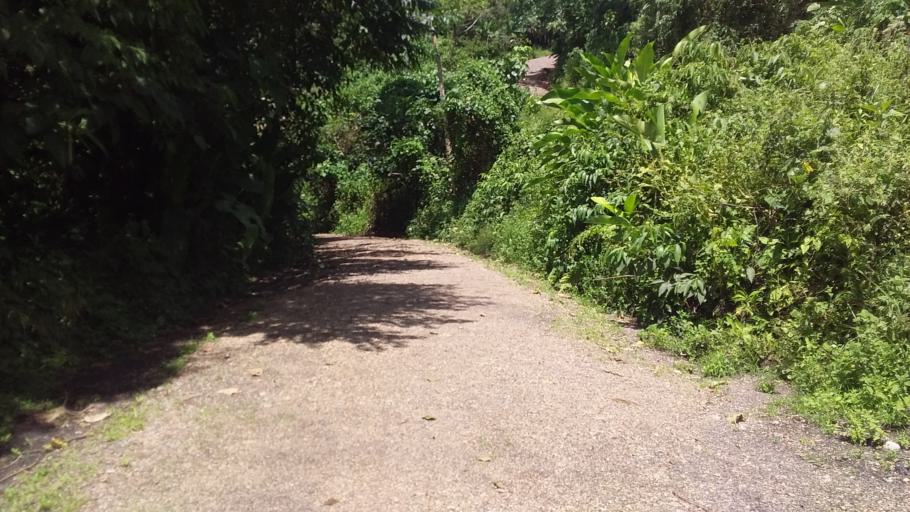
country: CO
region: Casanare
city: Nunchia
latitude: 5.6330
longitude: -72.3409
